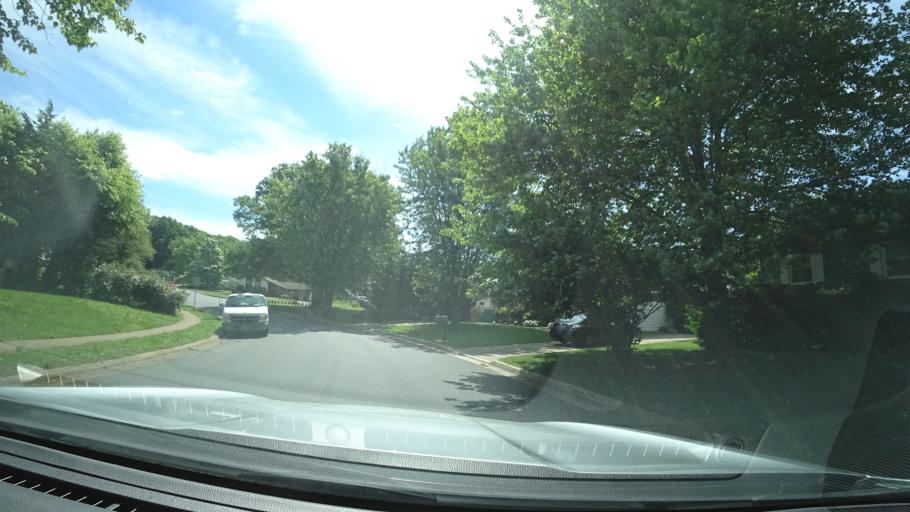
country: US
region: Virginia
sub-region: Loudoun County
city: Oak Grove
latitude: 38.9901
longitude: -77.4094
